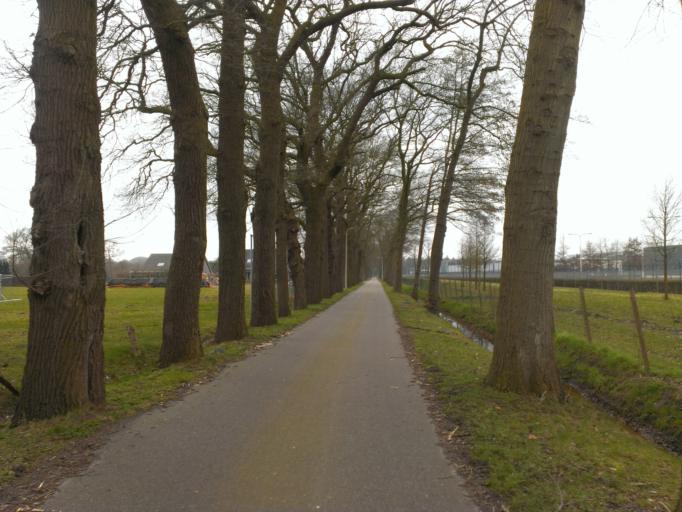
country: NL
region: Overijssel
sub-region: Gemeente Almelo
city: Almelo
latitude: 52.3341
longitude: 6.6959
